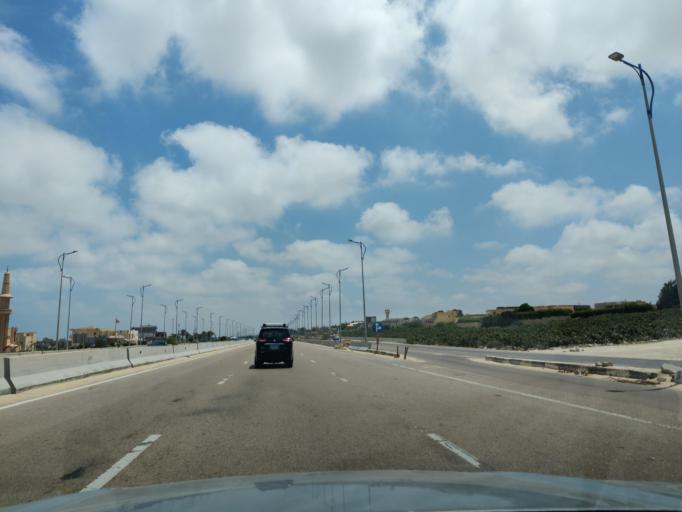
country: EG
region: Alexandria
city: Alexandria
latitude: 30.9669
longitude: 29.5559
